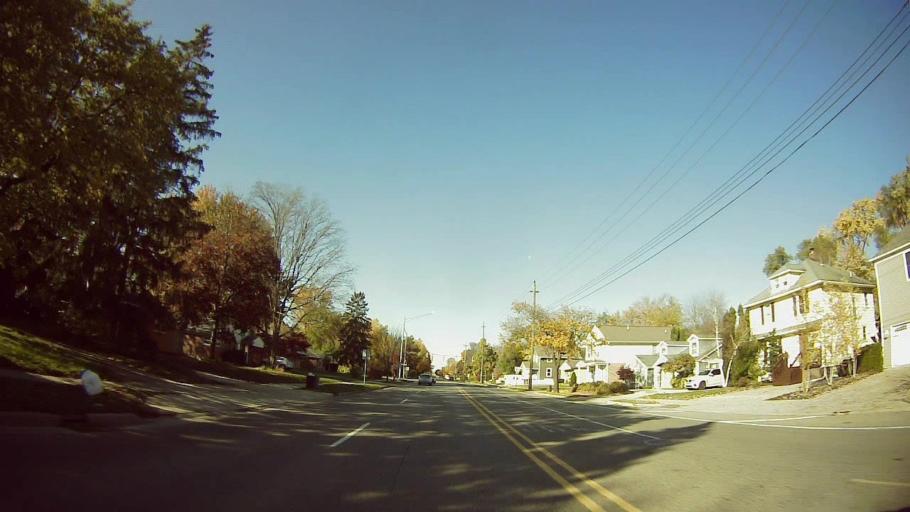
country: US
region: Michigan
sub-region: Oakland County
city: Birmingham
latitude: 42.5320
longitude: -83.2033
